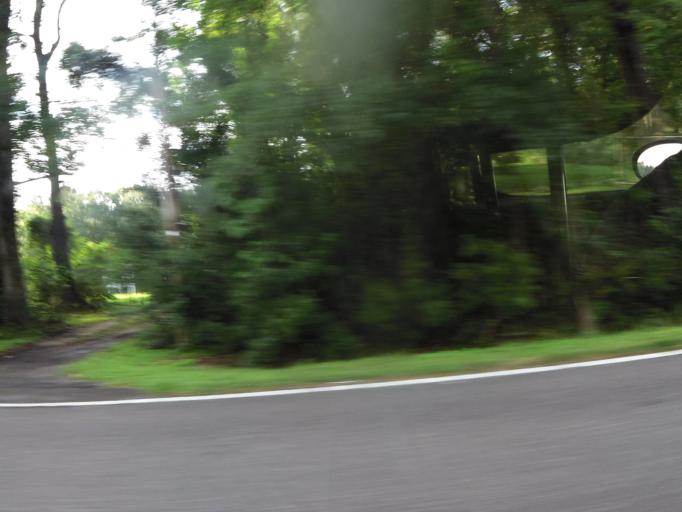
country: US
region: Florida
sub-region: Nassau County
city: Nassau Village-Ratliff
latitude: 30.4158
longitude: -81.7658
